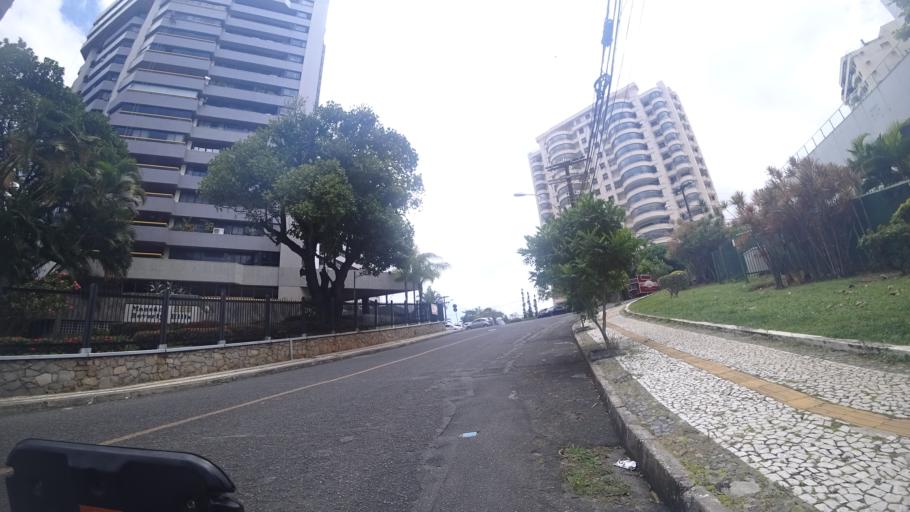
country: BR
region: Bahia
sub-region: Salvador
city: Salvador
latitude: -12.9949
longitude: -38.4733
